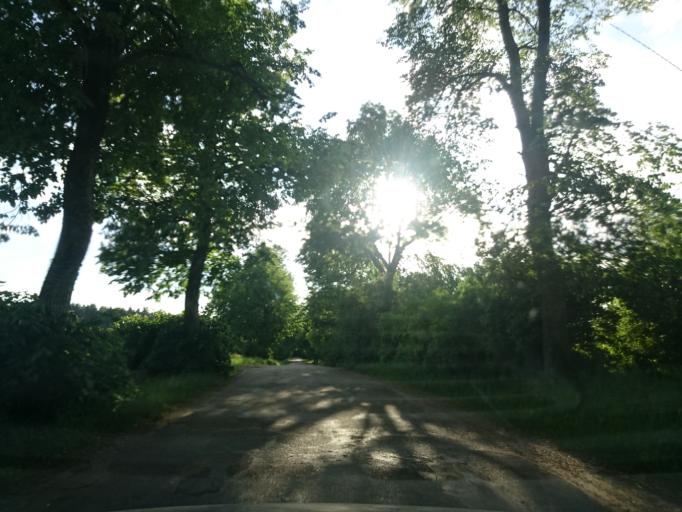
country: LV
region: Seja
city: Loja
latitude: 57.1226
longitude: 24.6458
